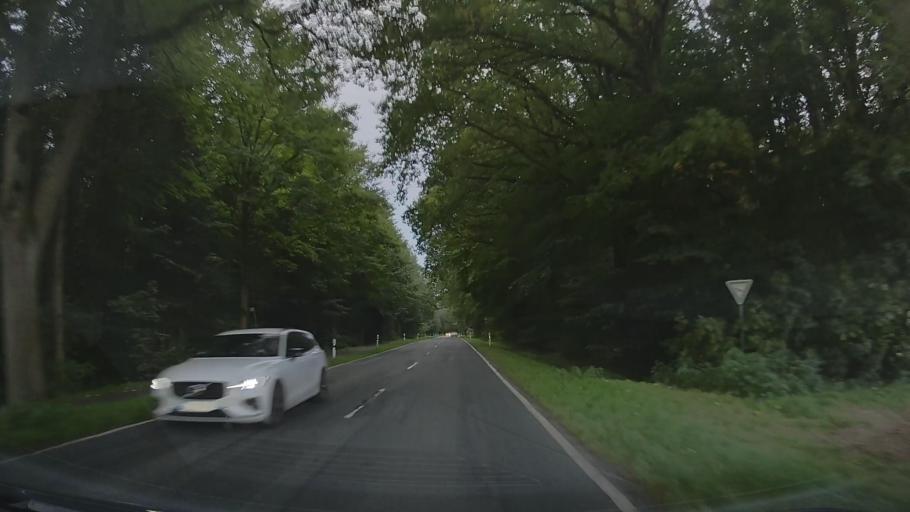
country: DE
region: Lower Saxony
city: Syke
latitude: 52.9090
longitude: 8.8632
